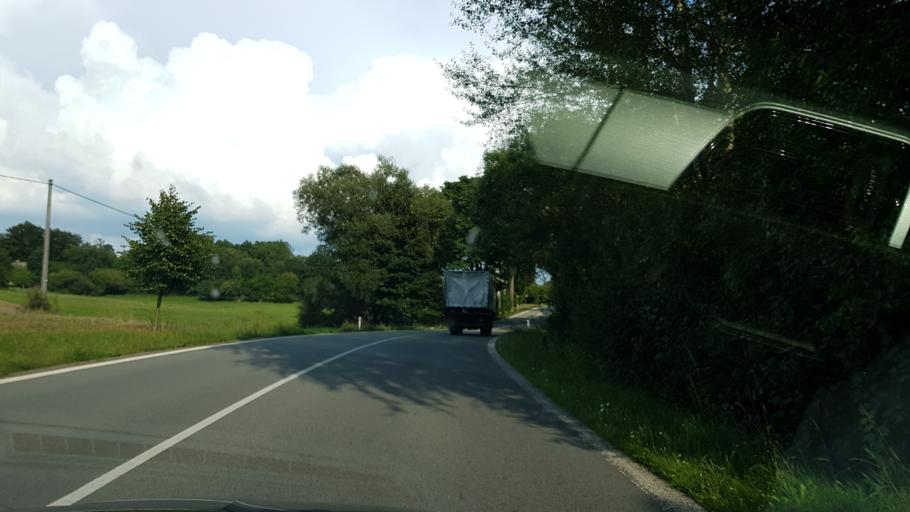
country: CZ
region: Pardubicky
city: Jablonne nad Orlici
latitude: 50.0903
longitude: 16.5929
